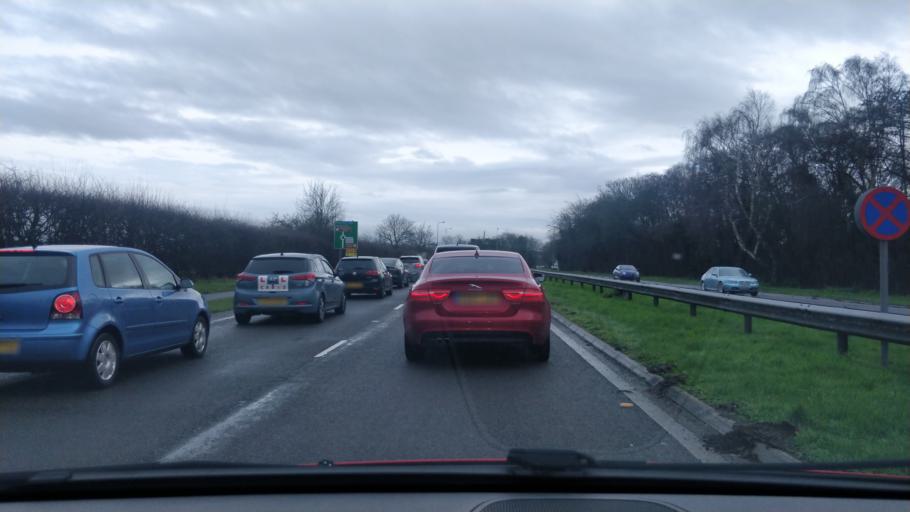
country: GB
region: England
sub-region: Sefton
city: Formby
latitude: 53.5707
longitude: -3.0492
